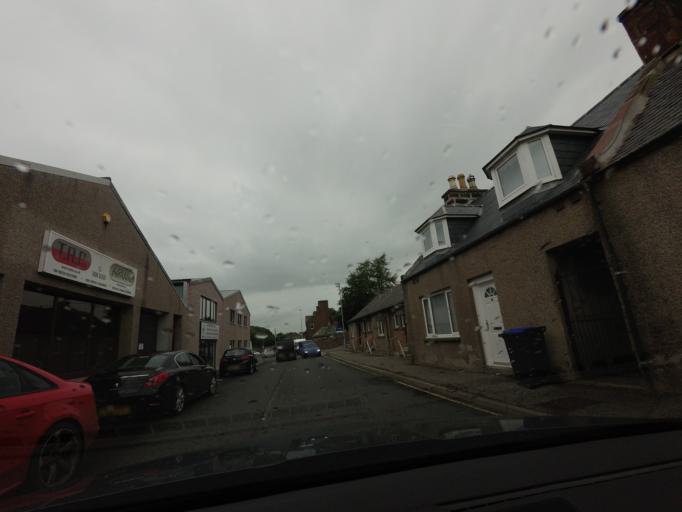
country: GB
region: Scotland
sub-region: Aberdeenshire
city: Turriff
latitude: 57.5389
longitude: -2.4623
